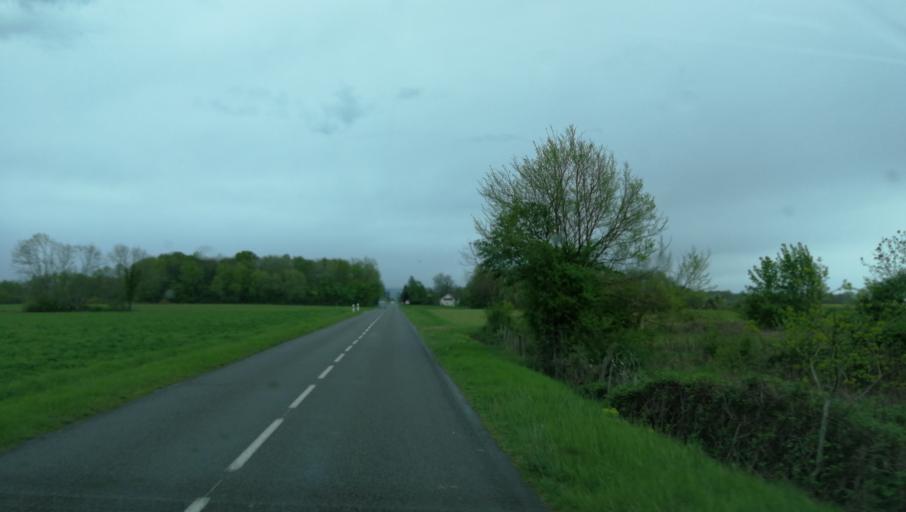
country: FR
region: Franche-Comte
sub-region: Departement du Jura
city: Bletterans
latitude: 46.7559
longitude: 5.4375
